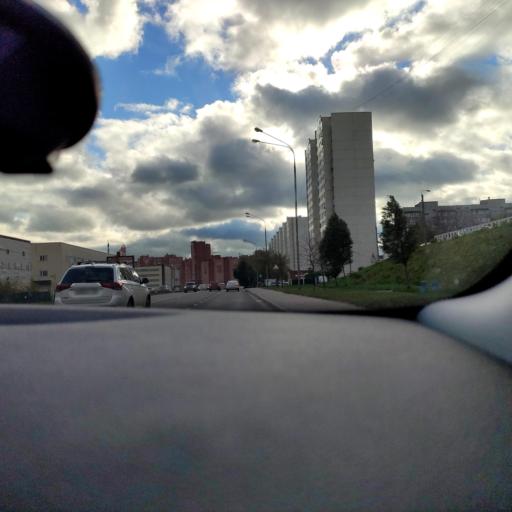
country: RU
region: Moskovskaya
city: Kotel'niki
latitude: 55.6366
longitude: 37.8484
